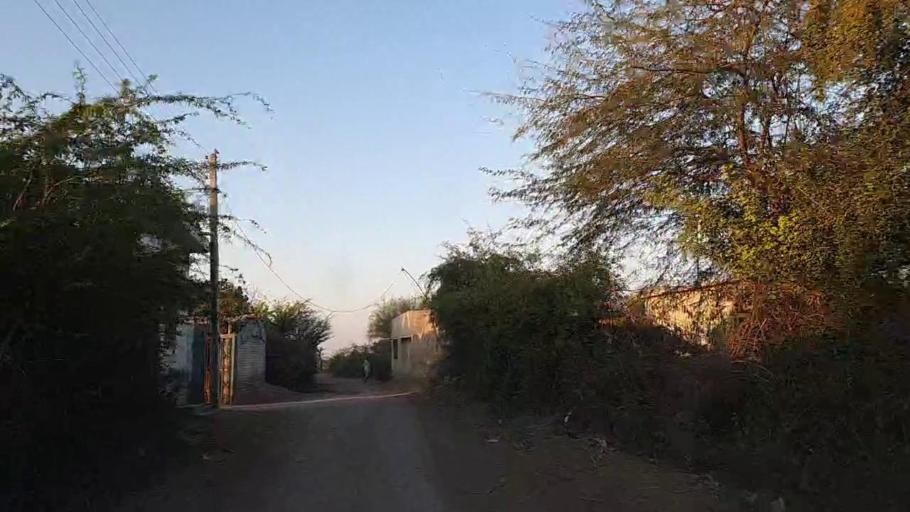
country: PK
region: Sindh
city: Samaro
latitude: 25.3025
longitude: 69.3970
